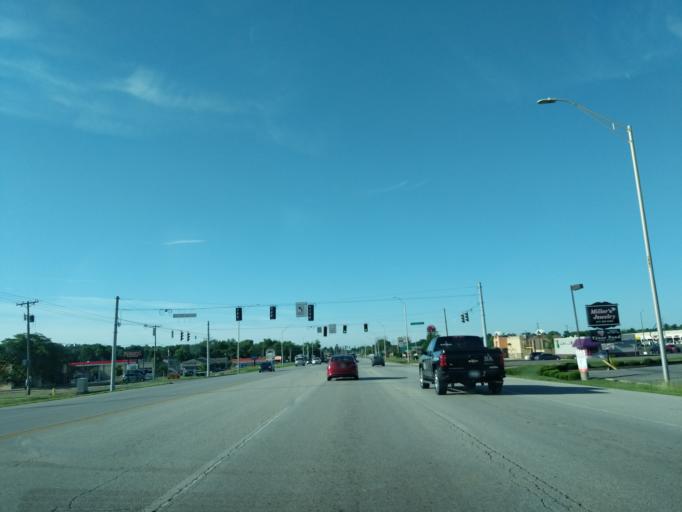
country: US
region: Indiana
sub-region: Hancock County
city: Greenfield
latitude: 39.8075
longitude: -85.7698
